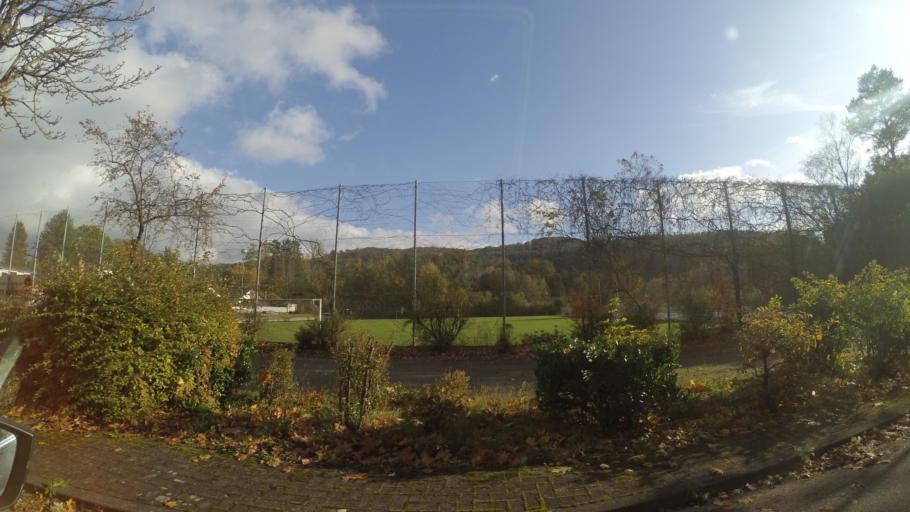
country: DE
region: Rheinland-Pfalz
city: Ruppertsweiler
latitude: 49.1924
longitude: 7.6746
